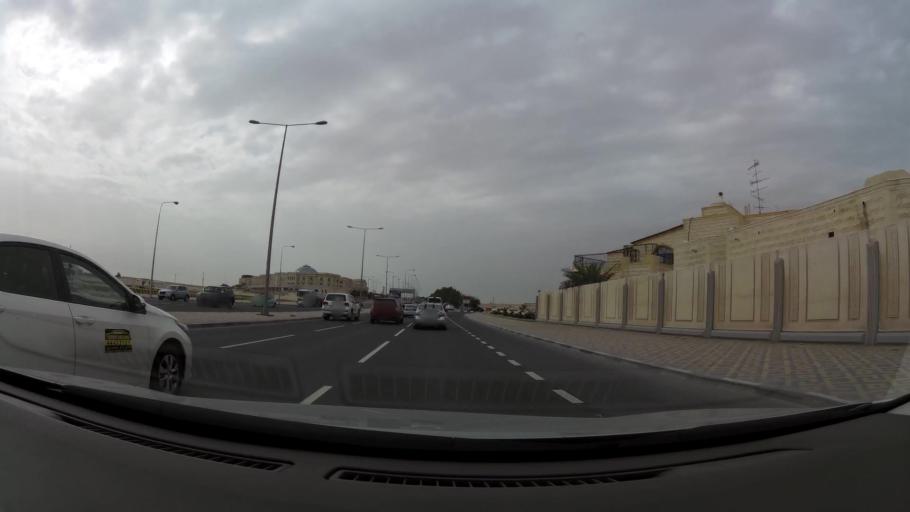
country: QA
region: Baladiyat ad Dawhah
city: Doha
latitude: 25.3302
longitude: 51.5028
